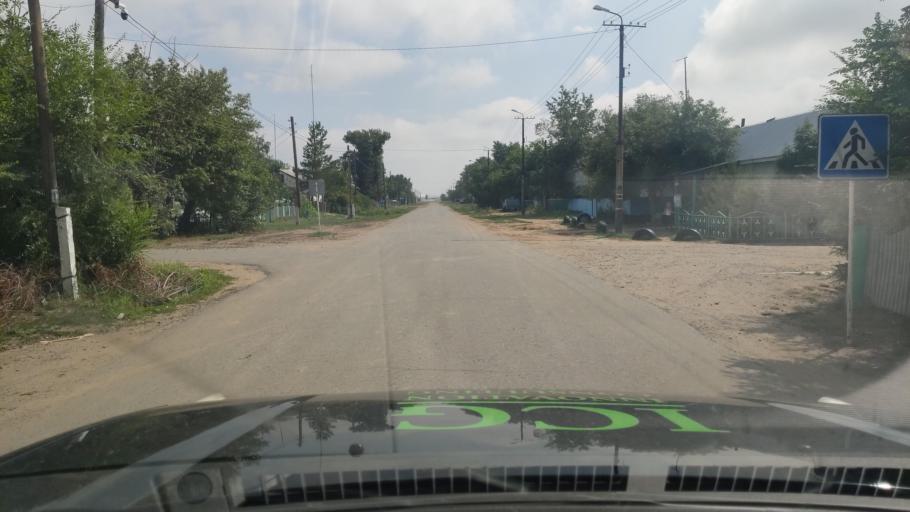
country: KZ
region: Pavlodar
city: Koktobe
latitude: 51.9657
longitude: 77.6406
